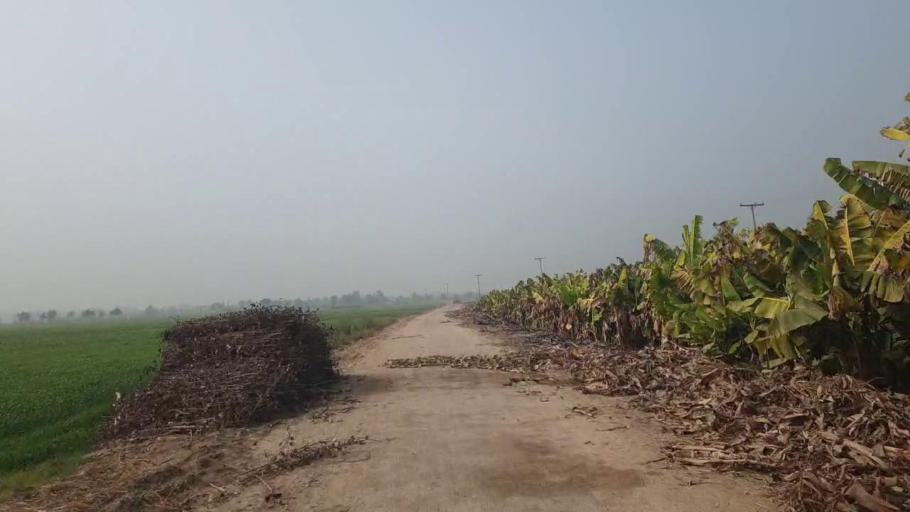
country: PK
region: Sindh
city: Bhit Shah
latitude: 25.8222
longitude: 68.5611
